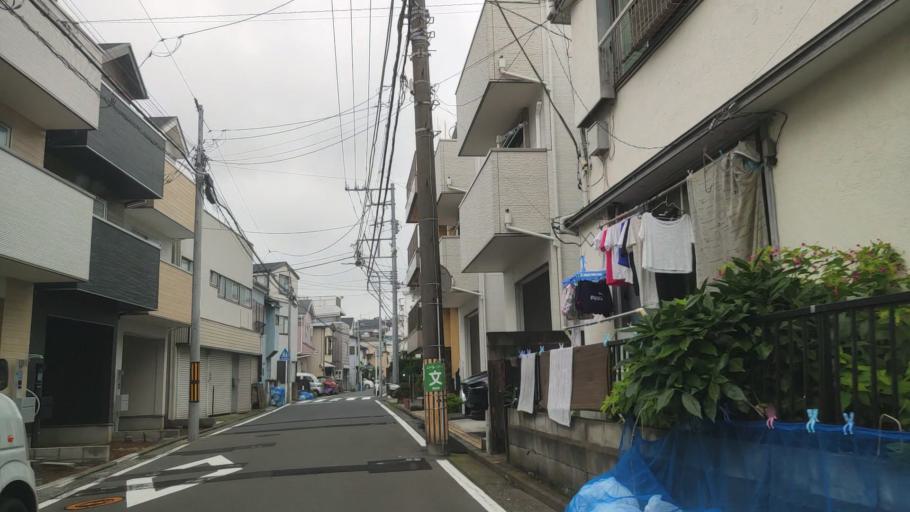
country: JP
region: Kanagawa
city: Yokohama
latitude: 35.4464
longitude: 139.6060
